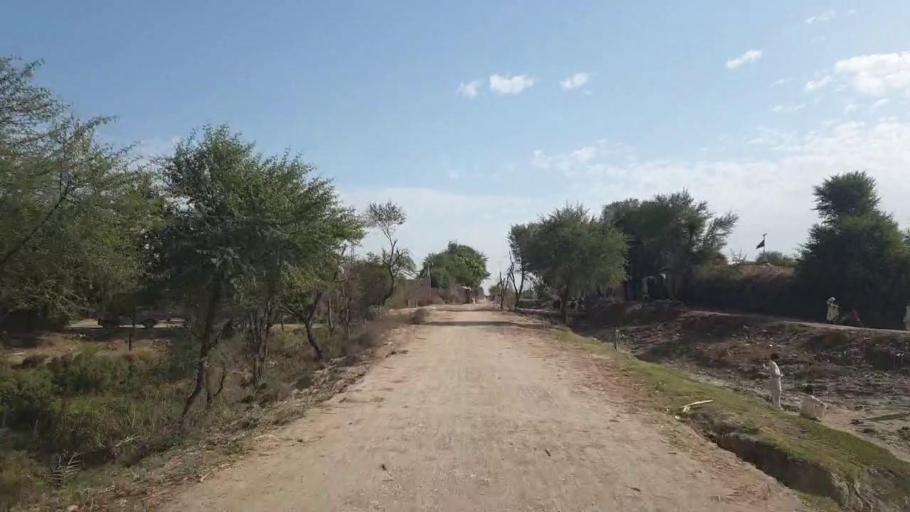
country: PK
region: Sindh
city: Shahdadpur
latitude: 26.0216
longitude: 68.4931
